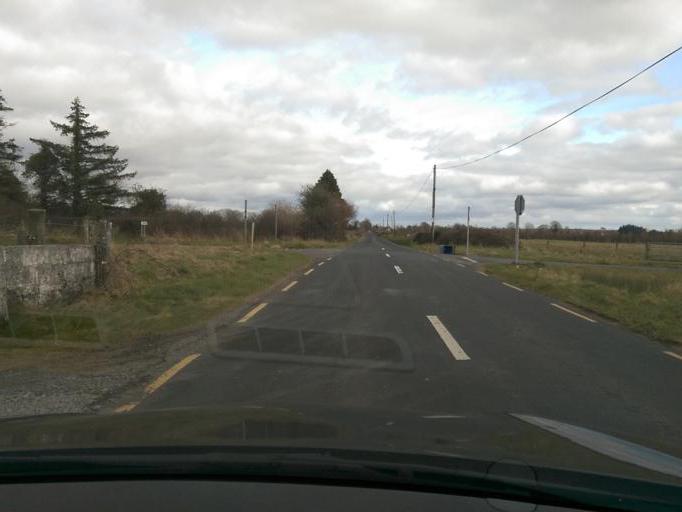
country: IE
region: Connaught
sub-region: County Galway
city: Ballinasloe
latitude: 53.3317
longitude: -8.3576
